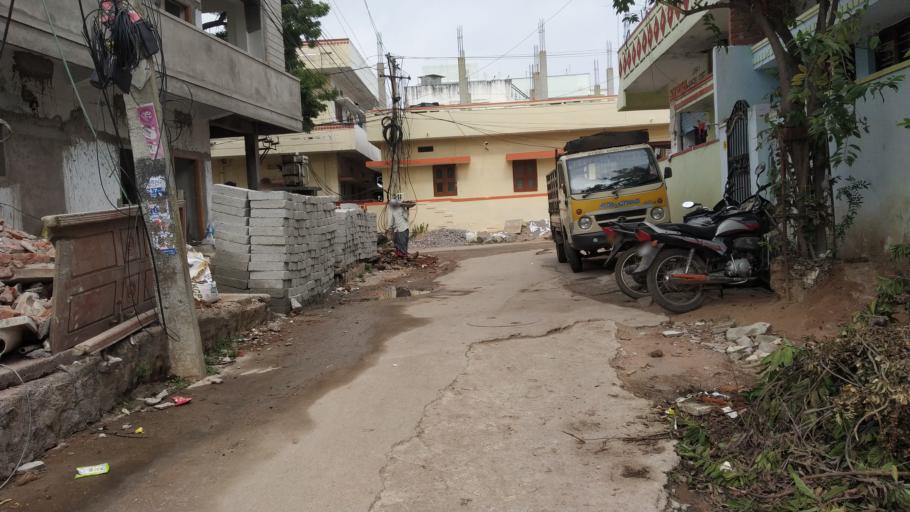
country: IN
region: Telangana
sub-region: Hyderabad
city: Malkajgiri
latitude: 17.4609
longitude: 78.5660
